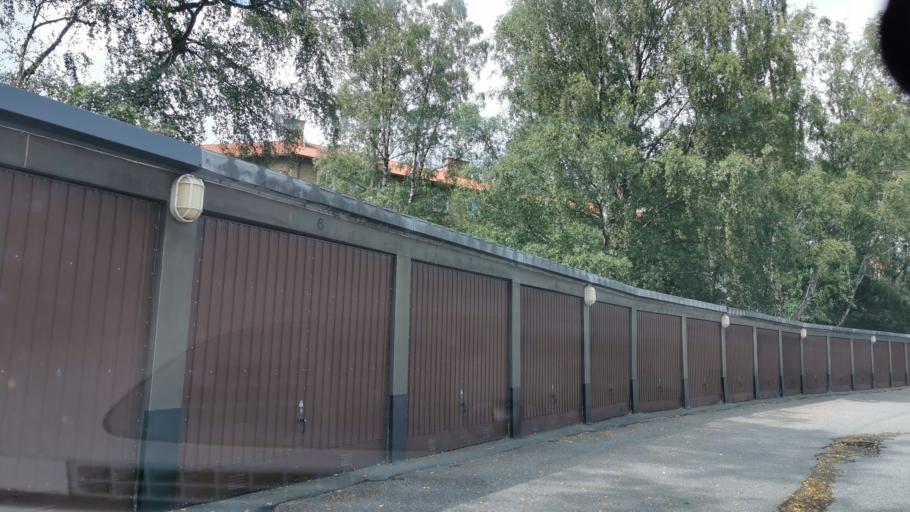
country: SE
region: Vaestra Goetaland
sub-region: Goteborg
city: Goeteborg
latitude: 57.6776
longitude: 11.9781
